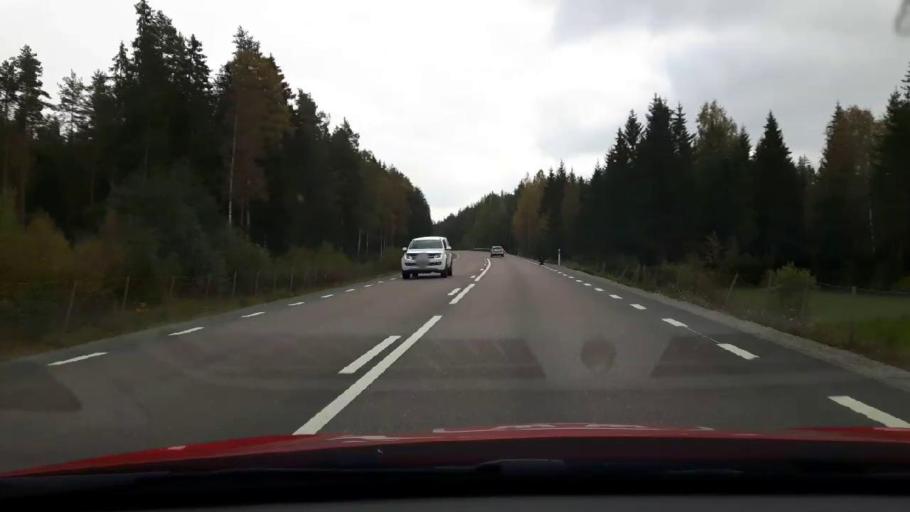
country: SE
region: Gaevleborg
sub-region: Bollnas Kommun
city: Bollnas
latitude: 61.3010
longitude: 16.4728
